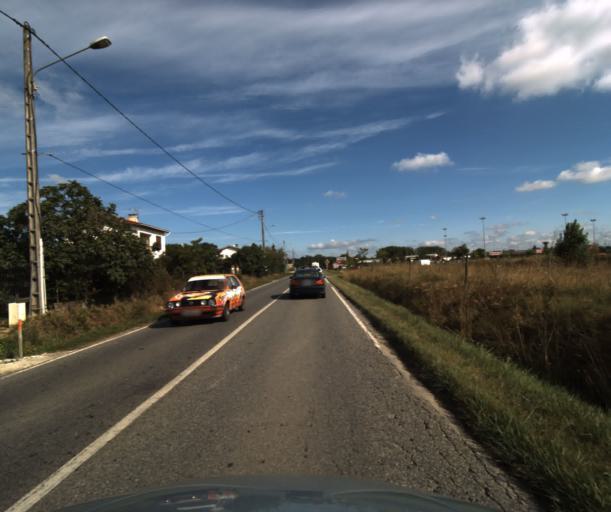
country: FR
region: Midi-Pyrenees
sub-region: Departement de la Haute-Garonne
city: Seysses
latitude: 43.4880
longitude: 1.3172
